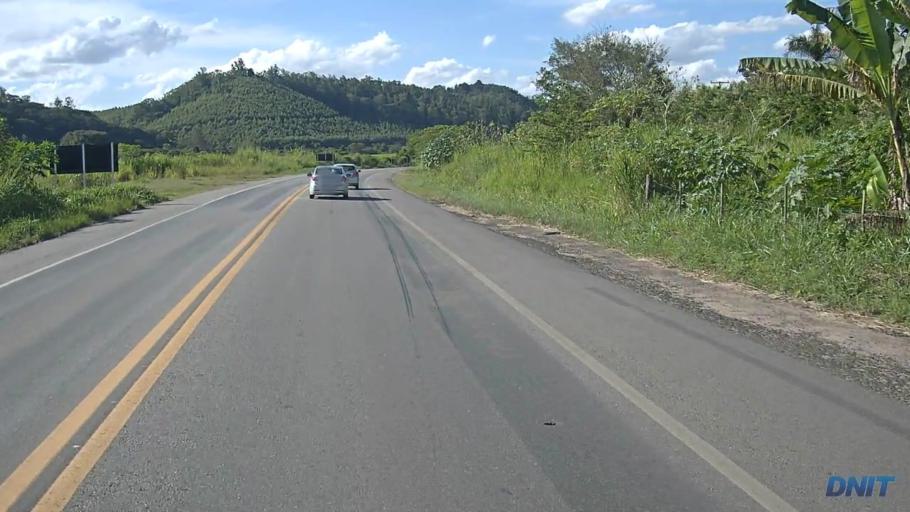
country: BR
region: Minas Gerais
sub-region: Belo Oriente
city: Belo Oriente
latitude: -19.2816
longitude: -42.3570
